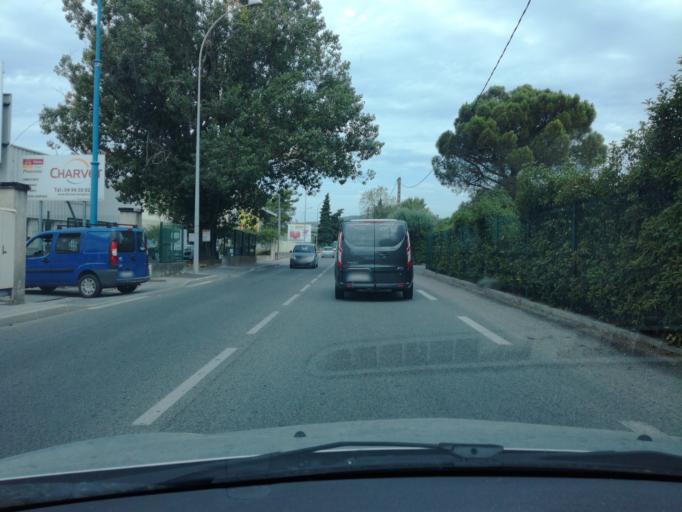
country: FR
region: Provence-Alpes-Cote d'Azur
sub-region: Departement du Var
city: Draguignan
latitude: 43.5230
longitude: 6.4634
